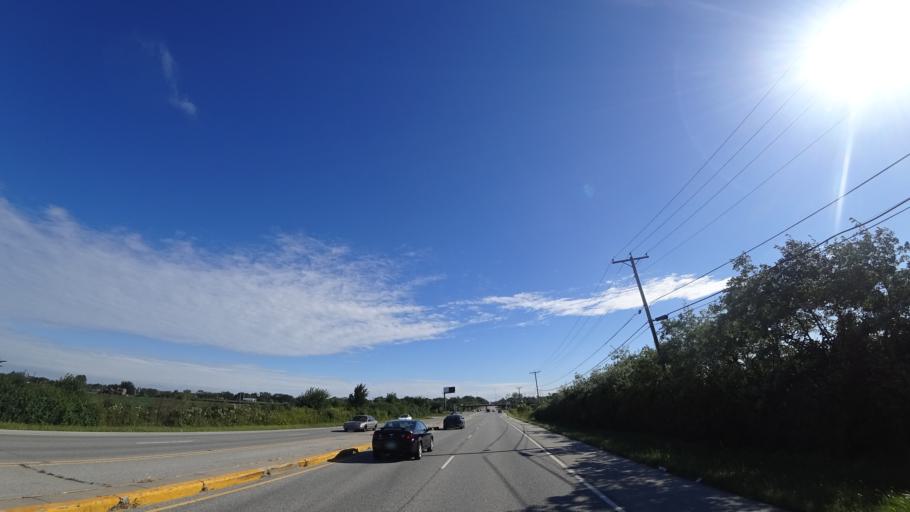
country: US
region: Illinois
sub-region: Cook County
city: Country Club Hills
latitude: 41.5742
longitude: -87.7333
